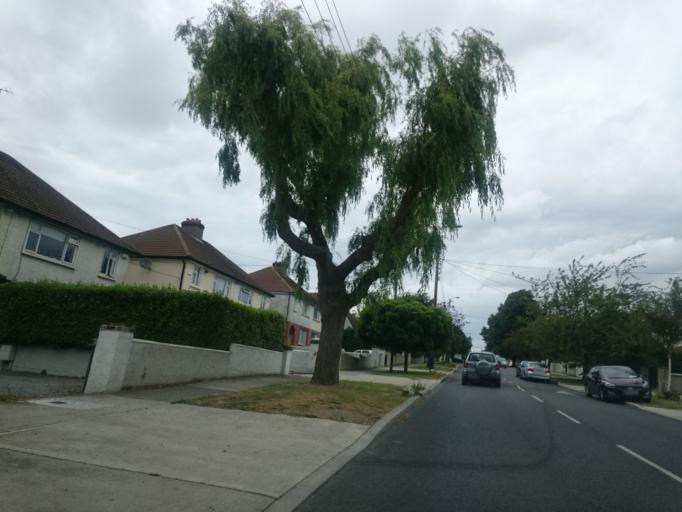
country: IE
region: Leinster
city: Mount Merrion
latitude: 53.2899
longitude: -6.2087
